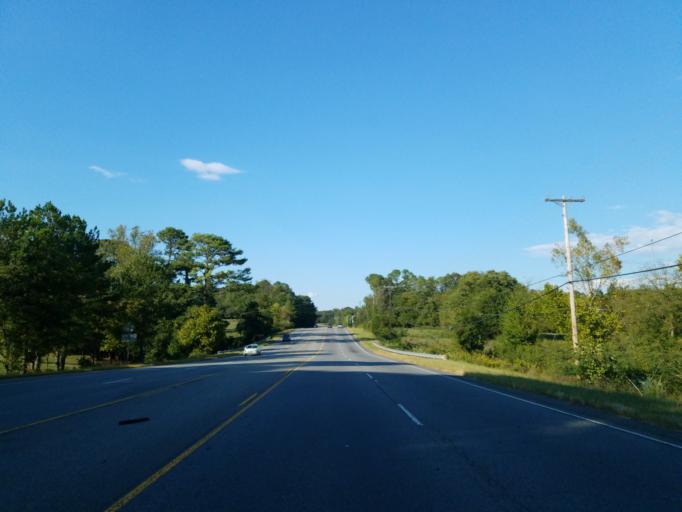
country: US
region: Georgia
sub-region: Murray County
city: Chatsworth
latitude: 34.8493
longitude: -84.7551
